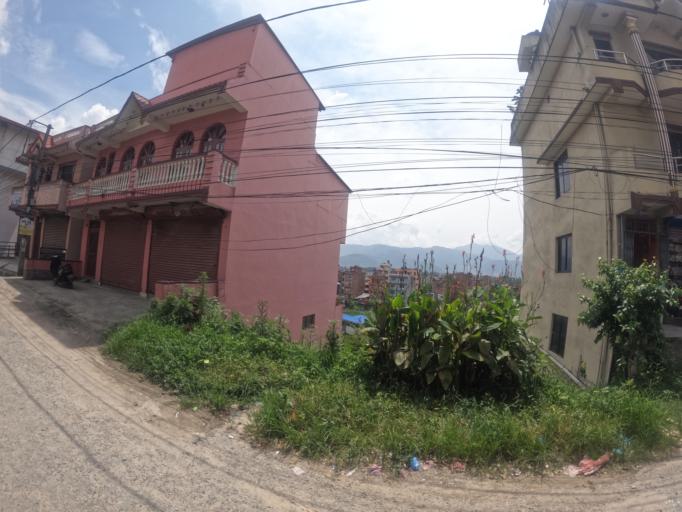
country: NP
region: Central Region
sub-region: Bagmati Zone
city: Bhaktapur
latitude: 27.6757
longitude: 85.3795
